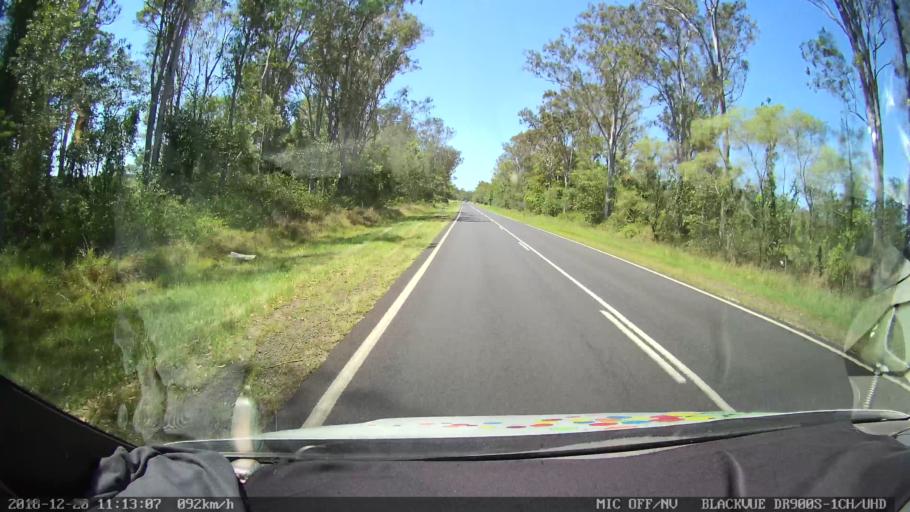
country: AU
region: New South Wales
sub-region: Richmond Valley
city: Casino
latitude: -28.9834
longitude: 153.0095
